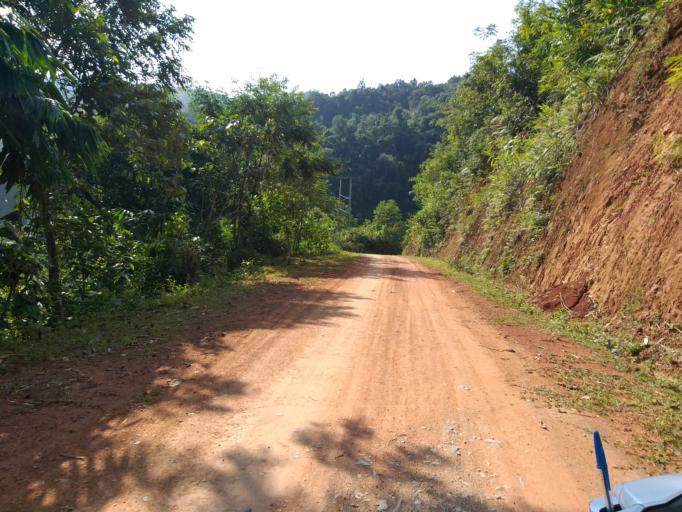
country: LA
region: Phongsali
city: Khoa
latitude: 21.1968
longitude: 102.6645
